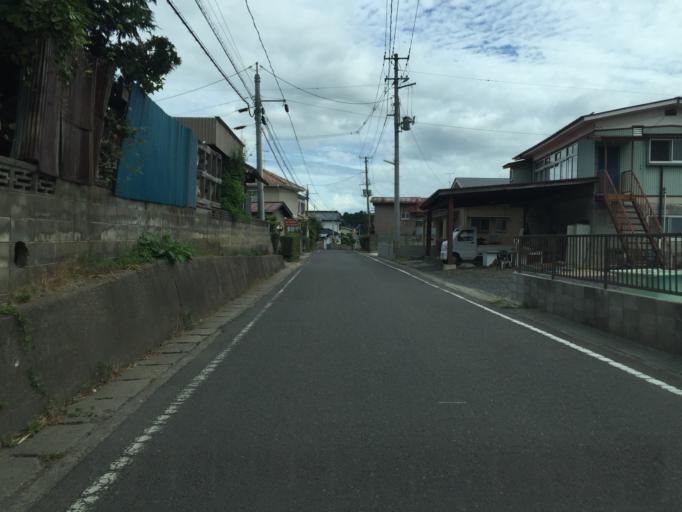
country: JP
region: Fukushima
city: Motomiya
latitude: 37.5356
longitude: 140.3628
